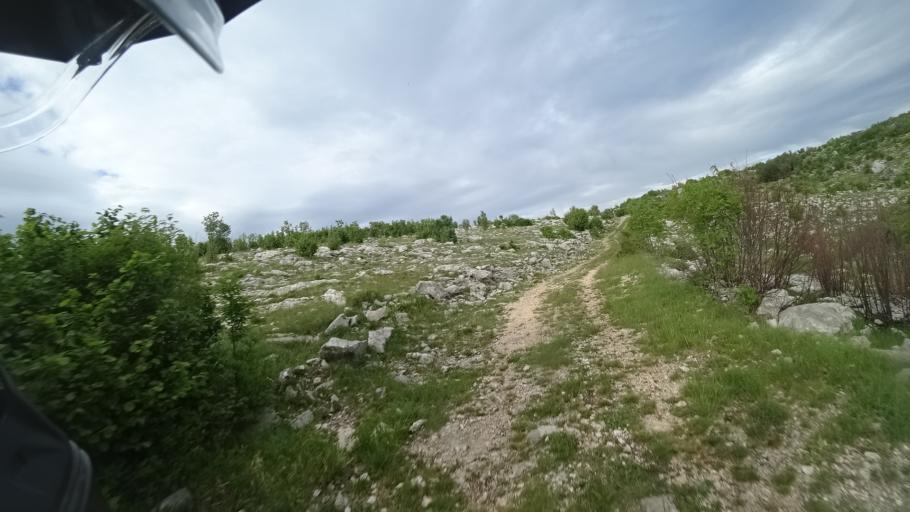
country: HR
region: Sibensko-Kniniska
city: Drnis
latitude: 43.8622
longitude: 16.3911
